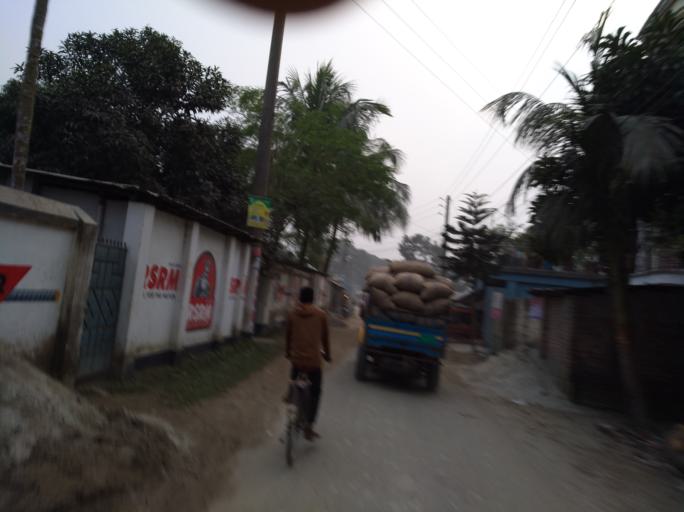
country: BD
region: Rajshahi
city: Saidpur
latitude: 25.9259
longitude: 88.8665
